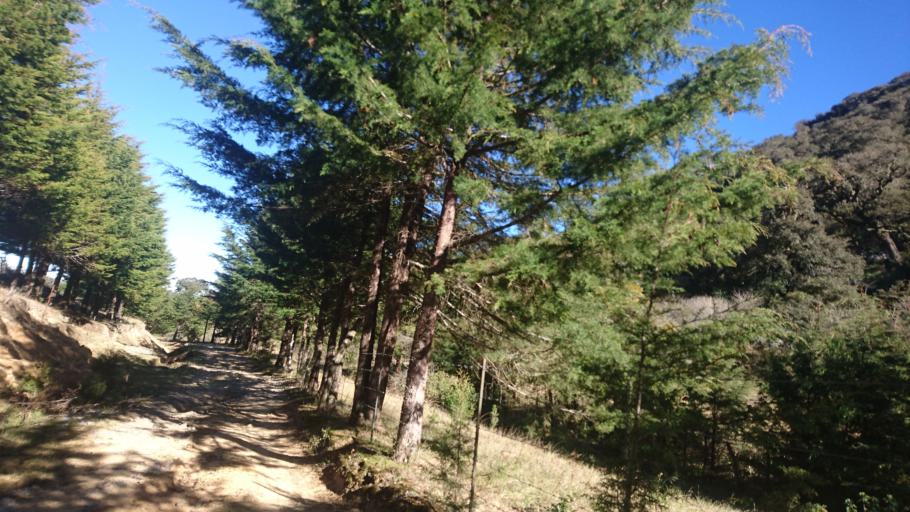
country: MX
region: San Luis Potosi
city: Zaragoza
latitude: 22.0185
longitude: -100.6061
